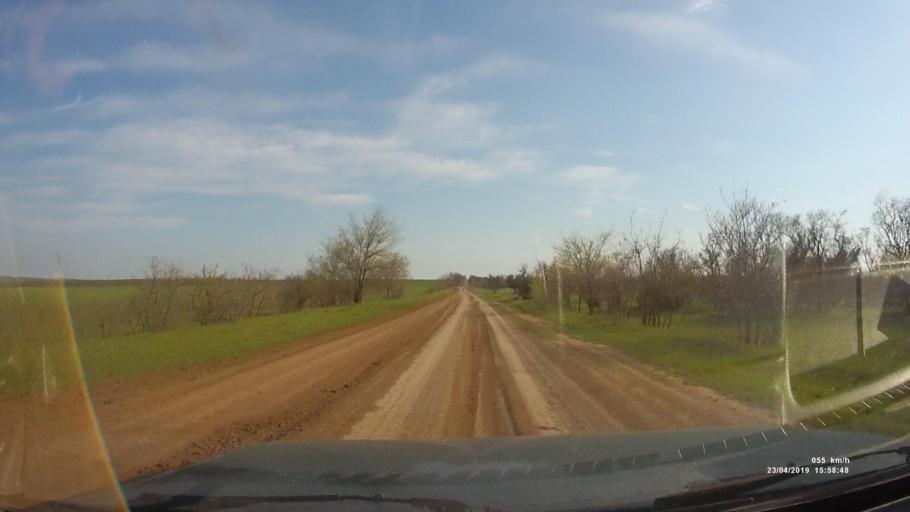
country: RU
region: Rostov
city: Remontnoye
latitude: 46.5213
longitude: 43.1095
